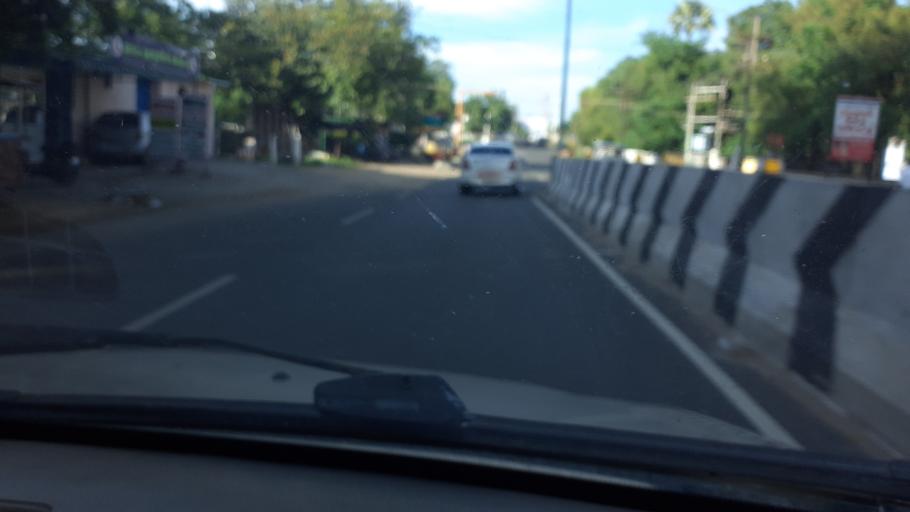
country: IN
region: Tamil Nadu
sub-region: Tirunelveli Kattabo
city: Tirunelveli
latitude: 8.7102
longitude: 77.7312
